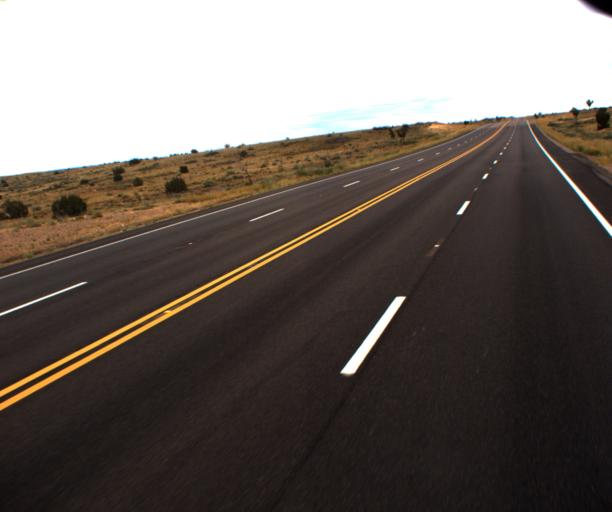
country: US
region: Arizona
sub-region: Navajo County
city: Snowflake
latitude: 34.5877
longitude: -110.0858
